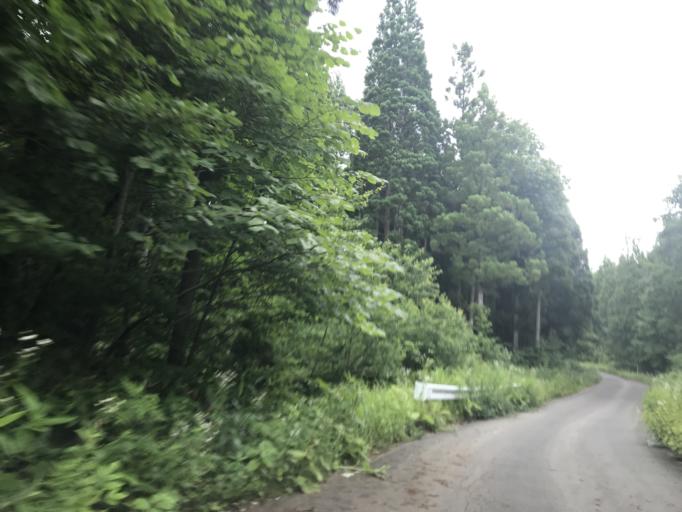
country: JP
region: Iwate
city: Ichinoseki
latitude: 38.9580
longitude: 140.8902
